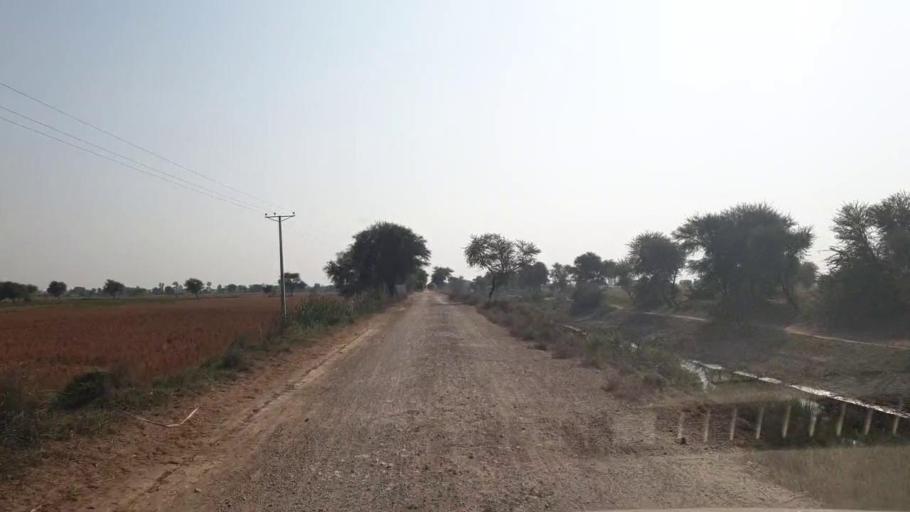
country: PK
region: Sindh
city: Kario
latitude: 24.9091
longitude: 68.6493
